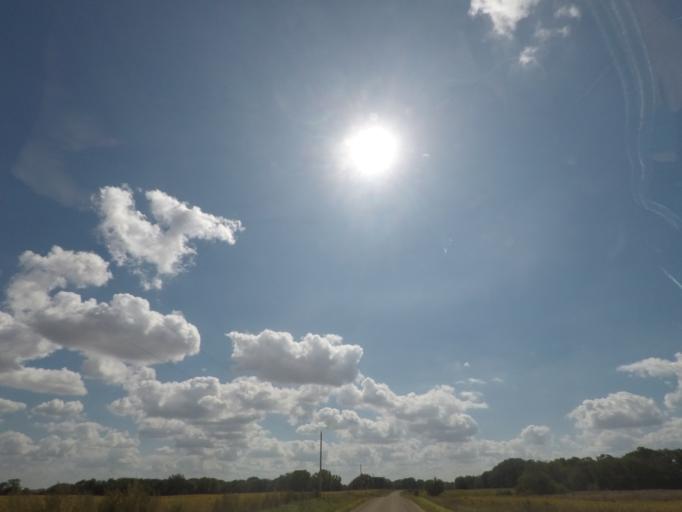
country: US
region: Iowa
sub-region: Story County
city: Nevada
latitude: 42.0759
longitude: -93.3511
